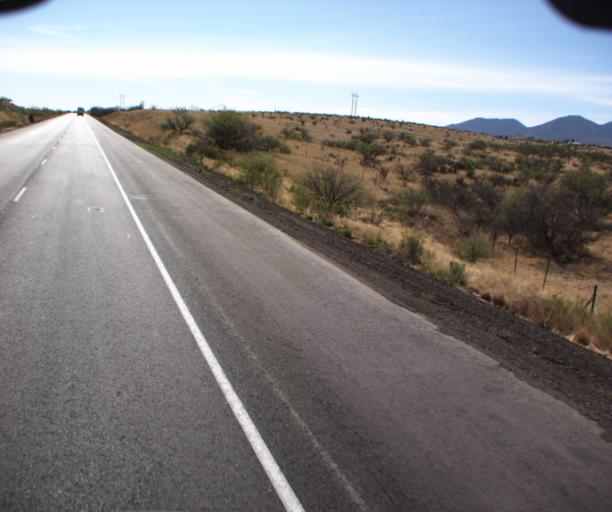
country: US
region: Arizona
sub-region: Cochise County
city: Mescal
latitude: 31.9667
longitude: -110.4648
